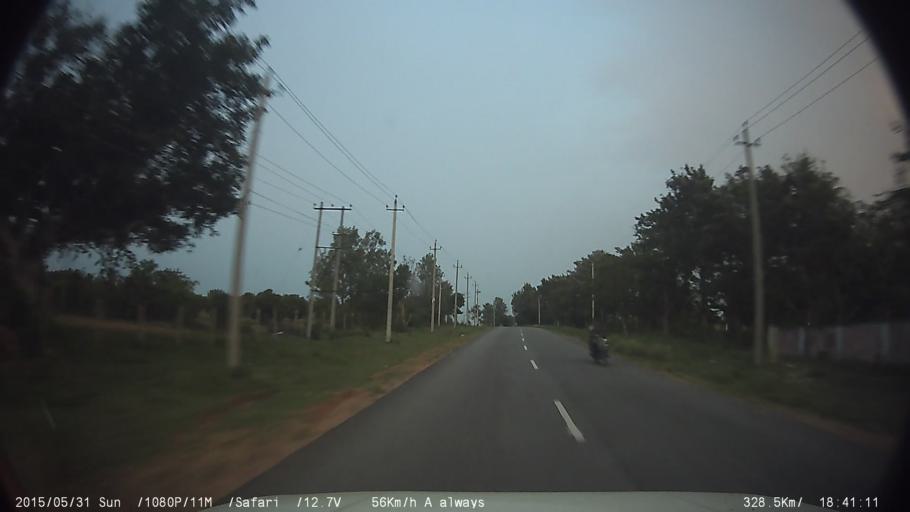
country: IN
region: Karnataka
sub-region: Mysore
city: Nanjangud
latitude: 12.1491
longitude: 76.7907
